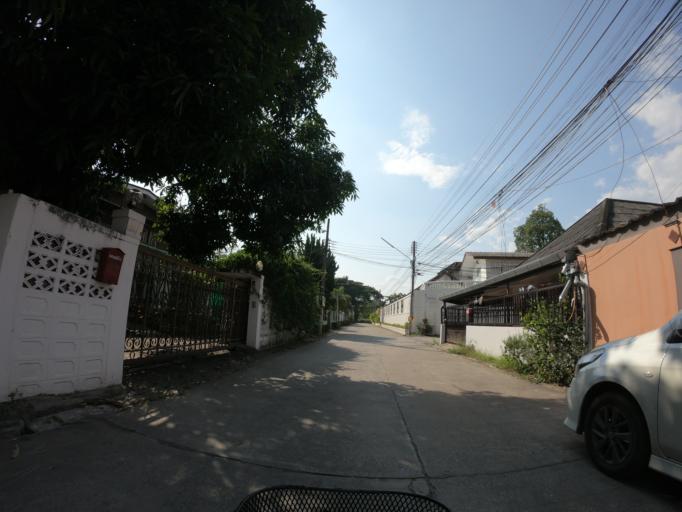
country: TH
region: Chiang Mai
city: Chiang Mai
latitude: 18.7934
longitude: 99.0154
